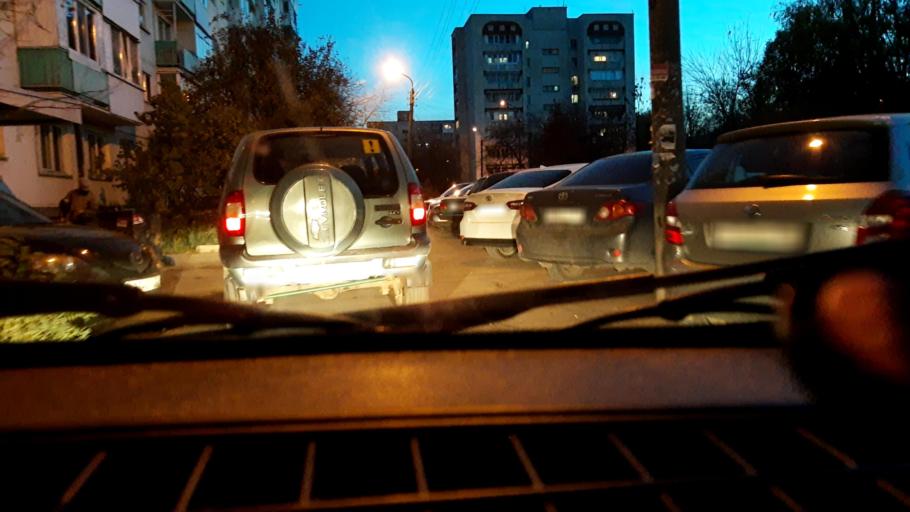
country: RU
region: Bashkortostan
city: Ufa
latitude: 54.7451
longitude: 56.0243
